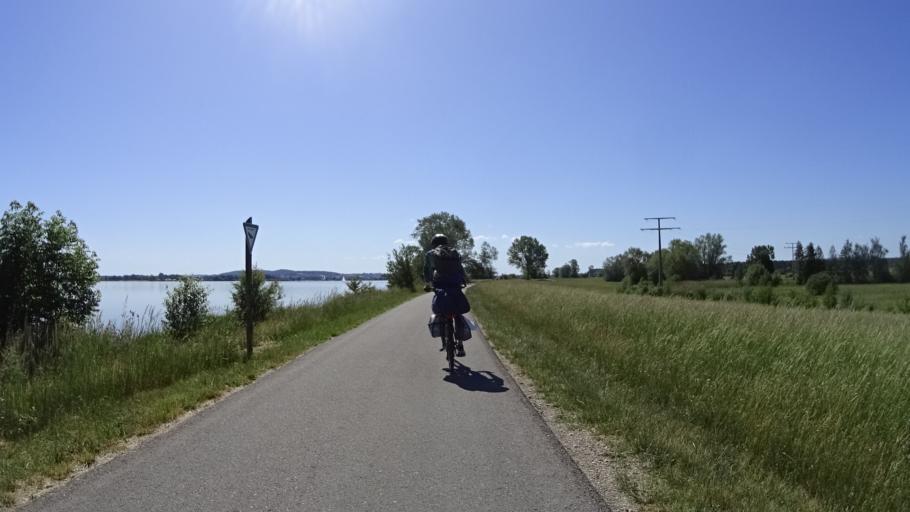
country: DE
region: Bavaria
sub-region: Regierungsbezirk Mittelfranken
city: Muhr am See
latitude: 49.1338
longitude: 10.7125
